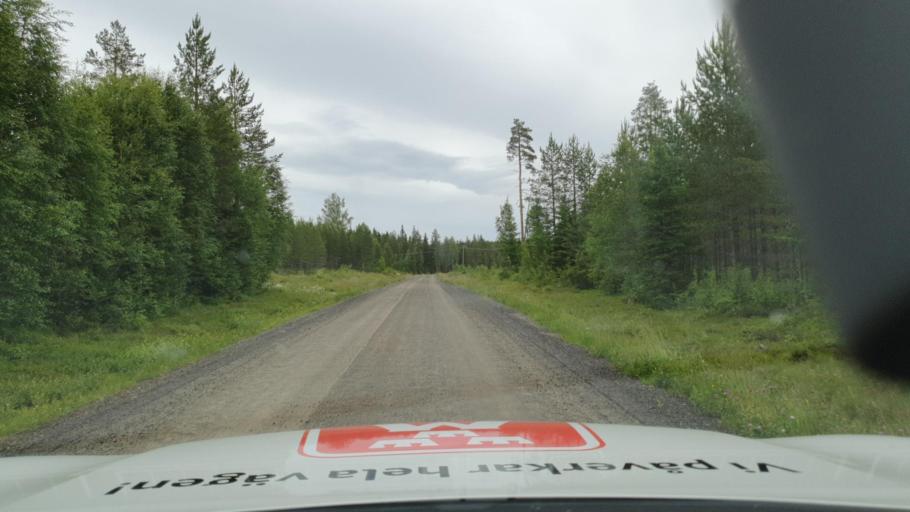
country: SE
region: Vaesterbotten
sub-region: Skelleftea Kommun
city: Burtraesk
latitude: 64.3552
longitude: 20.6143
